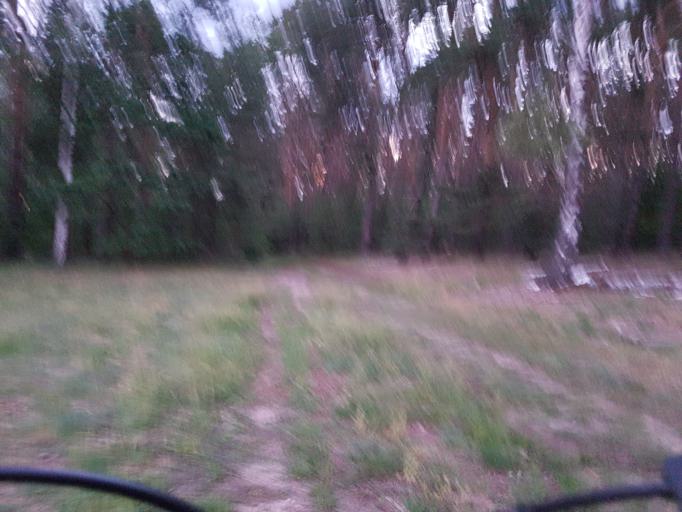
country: DE
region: Brandenburg
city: Schilda
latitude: 51.5609
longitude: 13.3654
